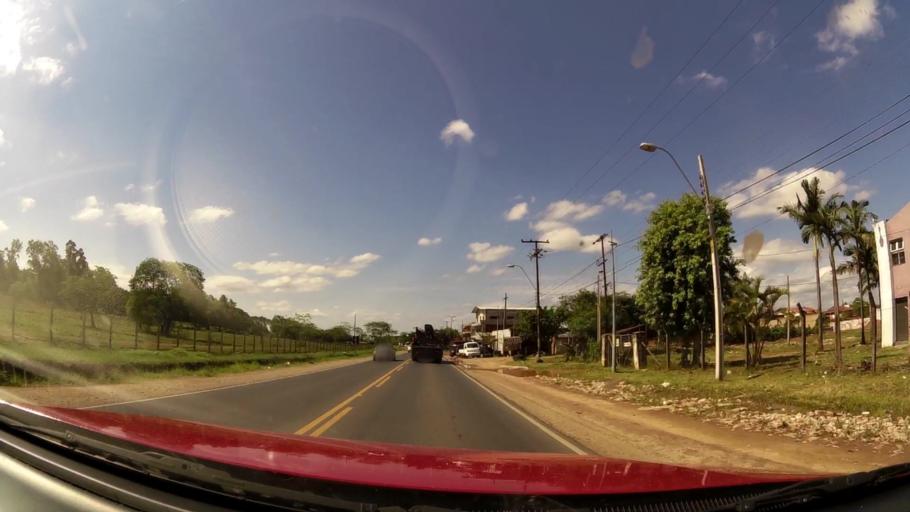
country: PY
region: Central
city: Fernando de la Mora
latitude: -25.2782
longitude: -57.5237
